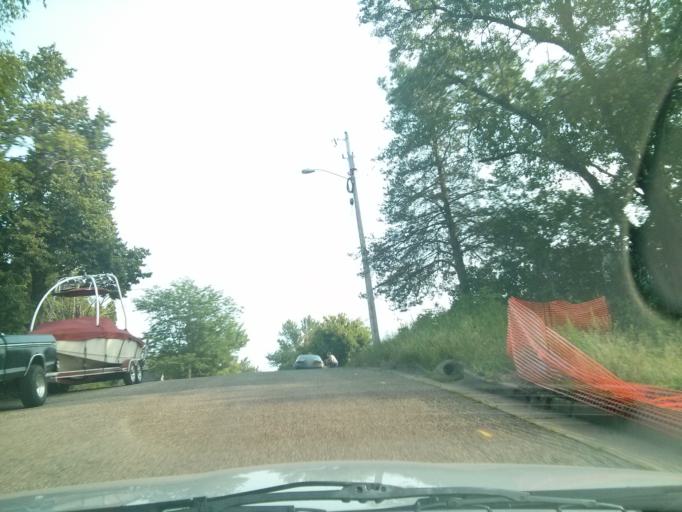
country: US
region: Wisconsin
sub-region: Saint Croix County
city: North Hudson
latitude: 44.9845
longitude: -92.7511
